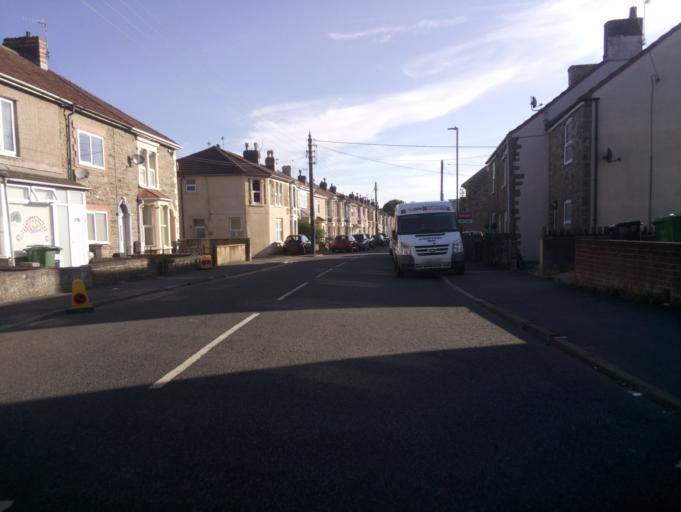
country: GB
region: England
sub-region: South Gloucestershire
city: Kingswood
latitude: 51.4565
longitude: -2.5084
